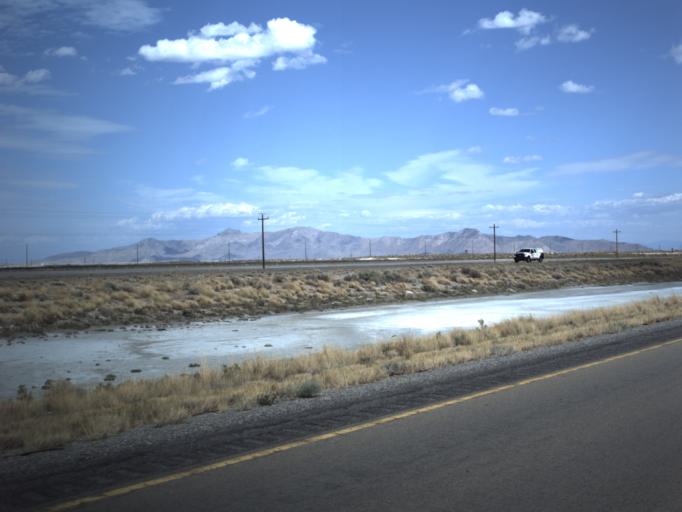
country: US
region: Utah
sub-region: Tooele County
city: Grantsville
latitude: 40.7504
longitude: -112.7011
